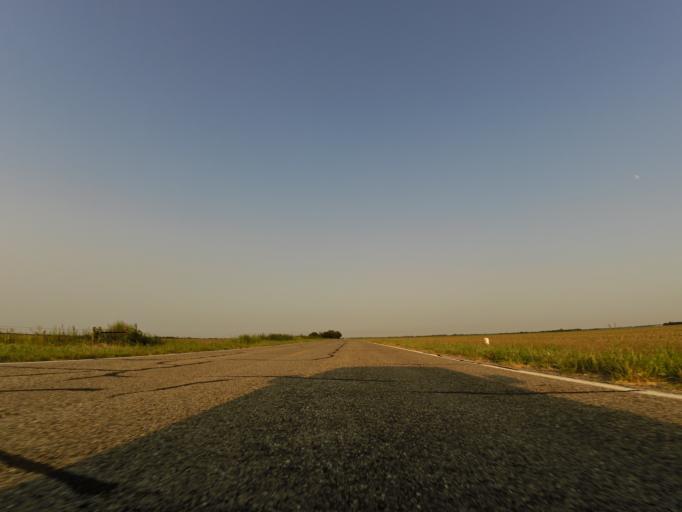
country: US
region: Kansas
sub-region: Reno County
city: South Hutchinson
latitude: 37.9699
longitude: -98.0052
